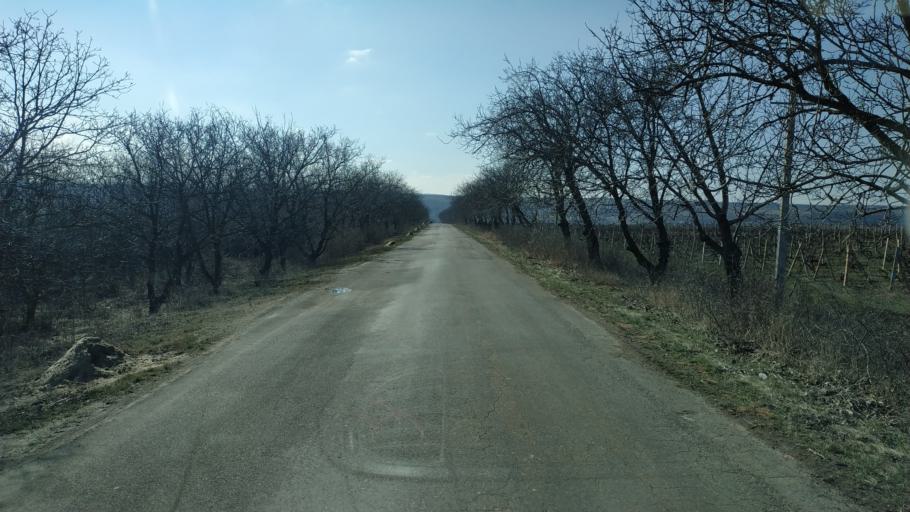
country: MD
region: Hincesti
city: Hincesti
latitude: 46.7622
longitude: 28.6687
